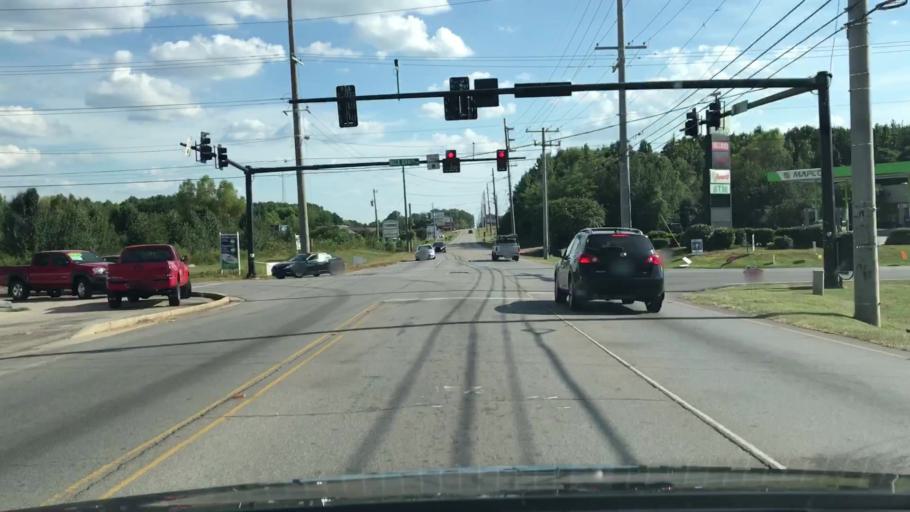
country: US
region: Alabama
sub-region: Madison County
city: Harvest
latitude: 34.8088
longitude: -86.7491
